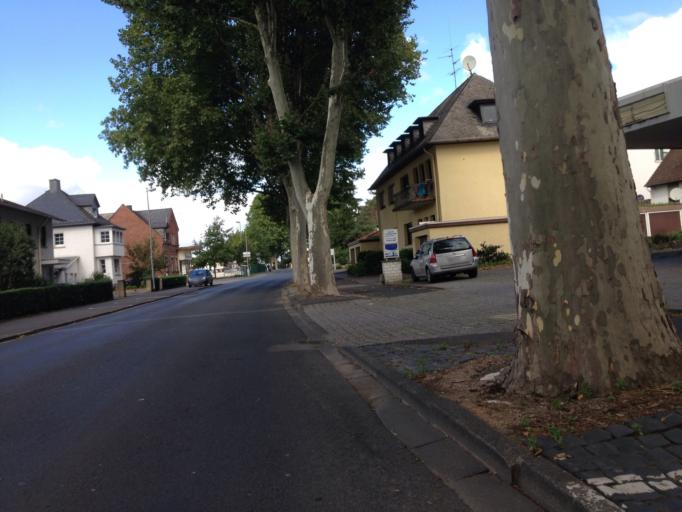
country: DE
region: Hesse
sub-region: Regierungsbezirk Giessen
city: Limburg an der Lahn
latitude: 50.3962
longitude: 8.0597
